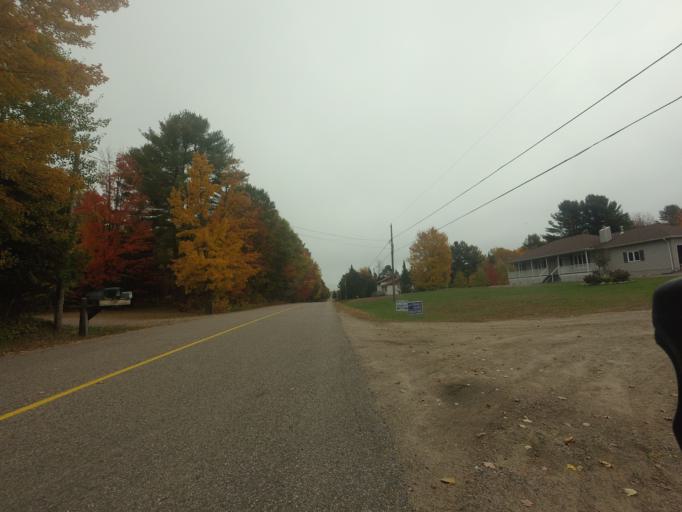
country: CA
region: Ontario
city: Petawawa
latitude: 45.7566
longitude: -77.2512
